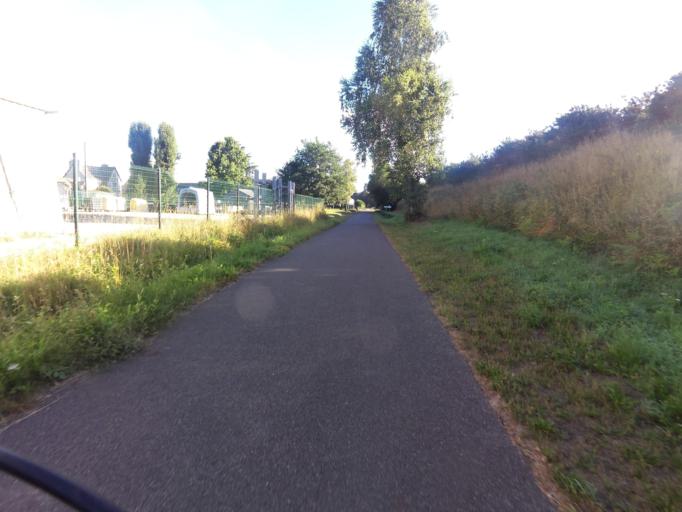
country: FR
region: Brittany
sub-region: Departement du Morbihan
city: Guillac
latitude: 47.8633
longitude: -2.4388
